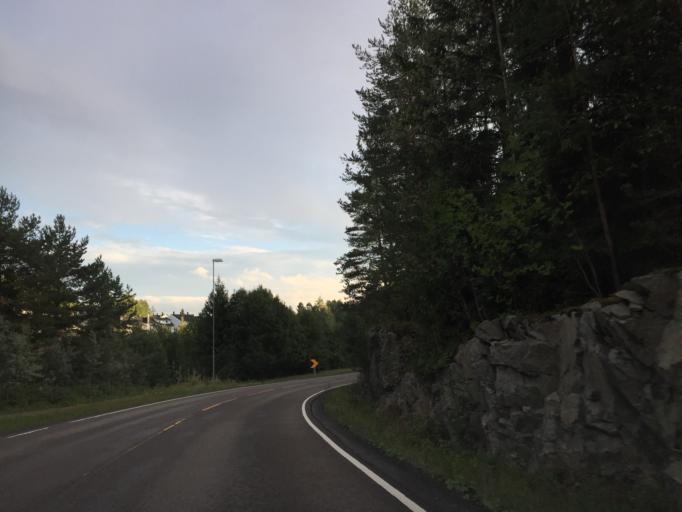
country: NO
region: Akershus
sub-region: Ski
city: Ski
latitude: 59.7682
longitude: 10.8483
